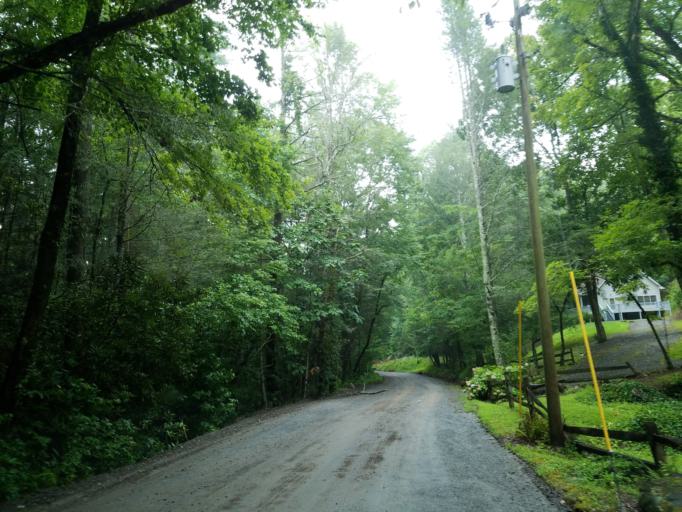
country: US
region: Georgia
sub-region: Fannin County
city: Blue Ridge
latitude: 34.7821
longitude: -84.3380
